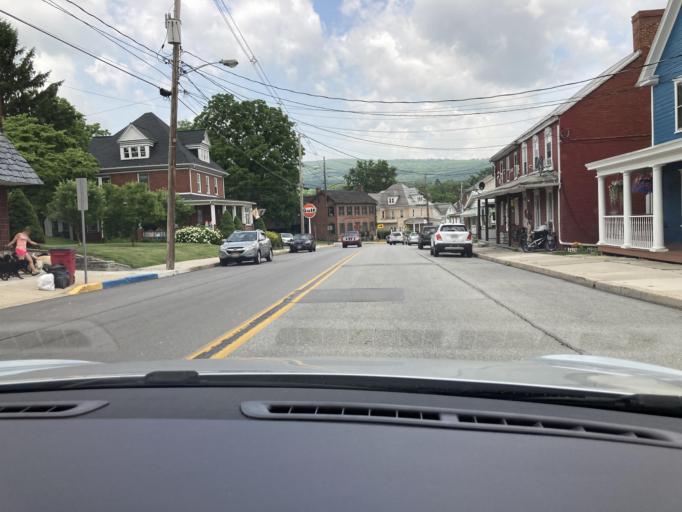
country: US
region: Pennsylvania
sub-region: Bedford County
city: Bedford
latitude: 40.0189
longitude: -78.5066
